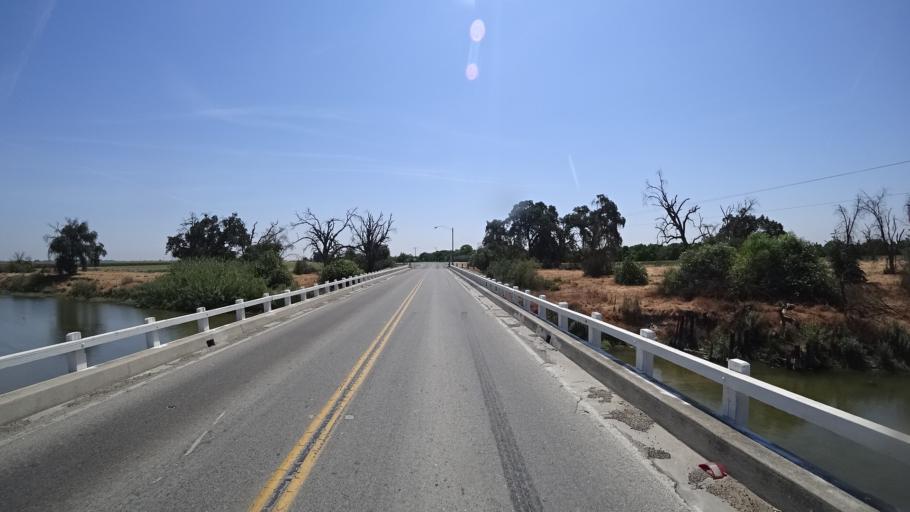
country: US
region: California
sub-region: Fresno County
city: Laton
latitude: 36.4015
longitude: -119.7517
